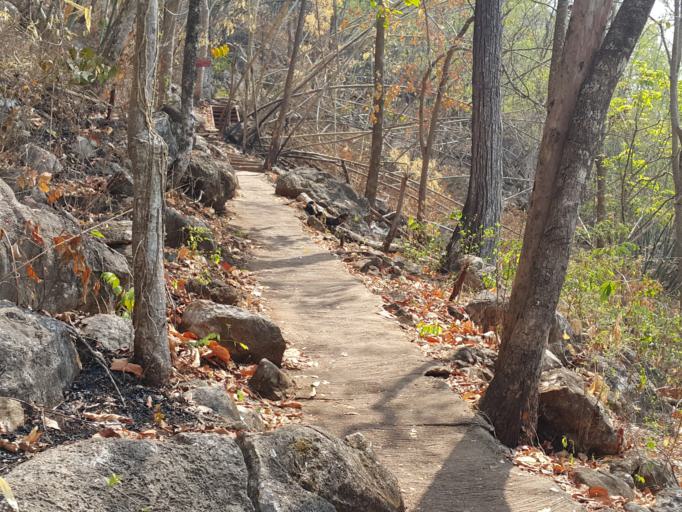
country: TH
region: Lampang
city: Mueang Pan
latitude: 18.7475
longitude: 99.5306
